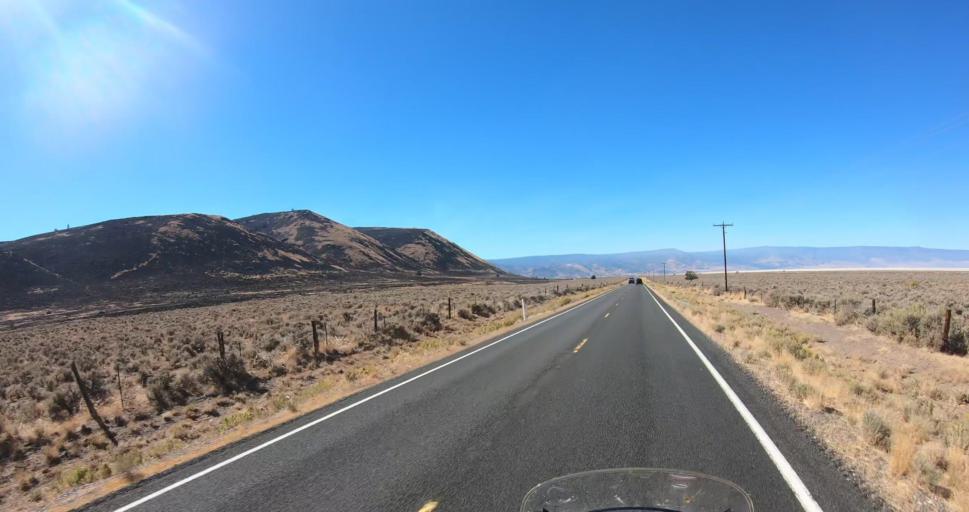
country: US
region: Oregon
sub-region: Lake County
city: Lakeview
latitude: 42.7211
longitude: -120.5982
